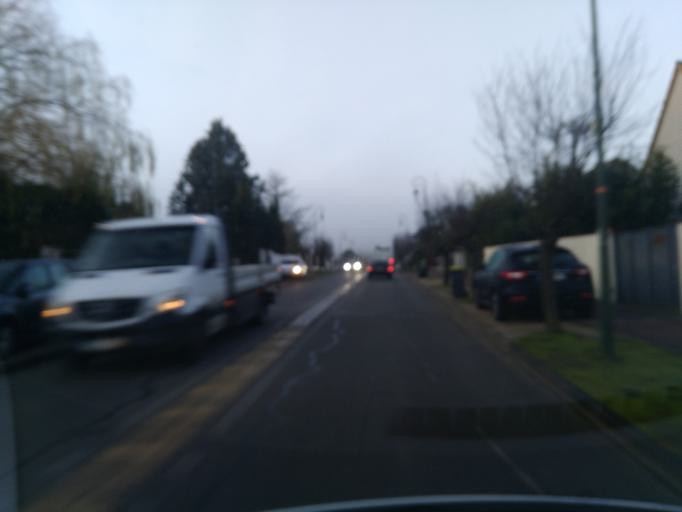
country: FR
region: Ile-de-France
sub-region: Departement des Yvelines
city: Orgeval
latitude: 48.9270
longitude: 1.9794
